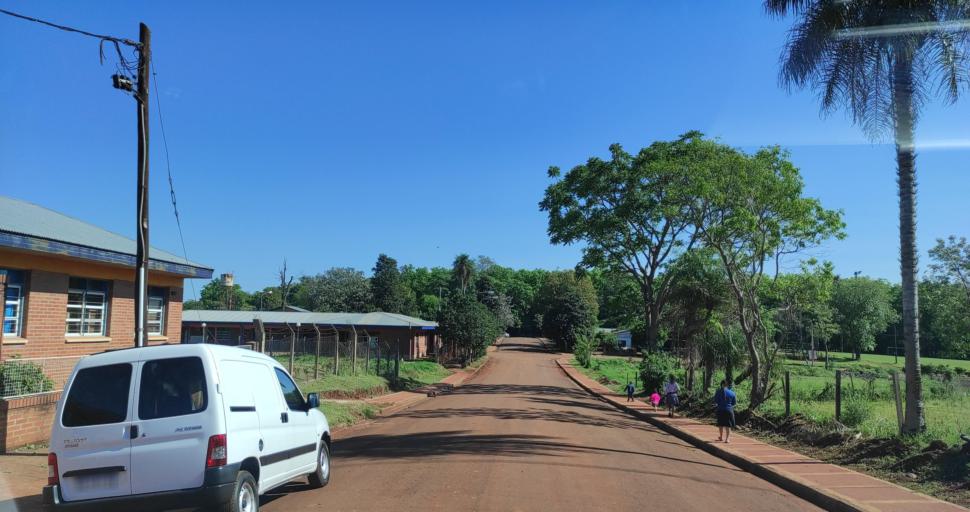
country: AR
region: Misiones
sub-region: Departamento de Candelaria
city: Loreto
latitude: -27.3322
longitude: -55.5249
